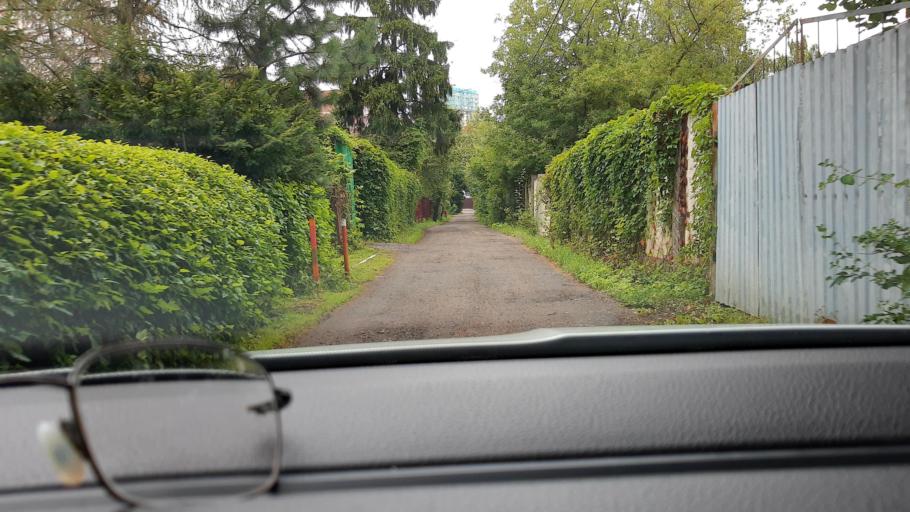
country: RU
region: Moskovskaya
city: Opalikha
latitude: 55.8304
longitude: 37.2897
